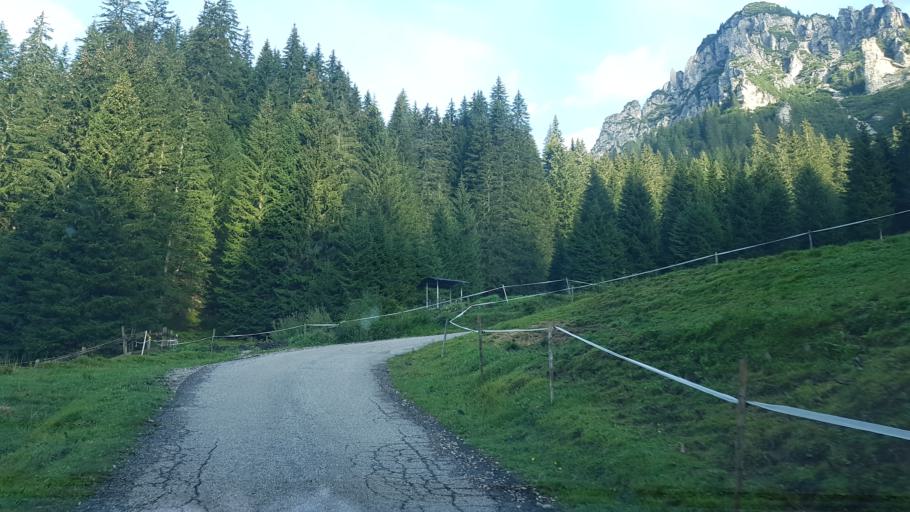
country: IT
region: Veneto
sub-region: Provincia di Belluno
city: San Pietro di Cadore
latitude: 46.6025
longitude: 12.5881
